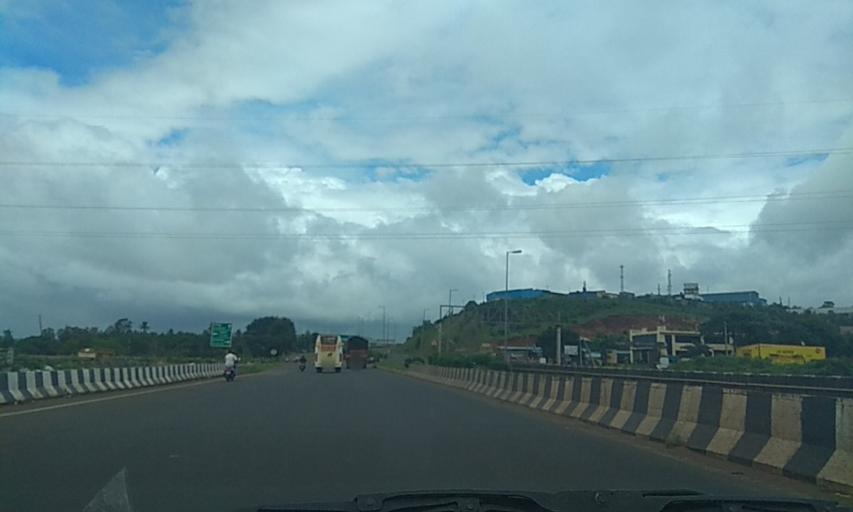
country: IN
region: Karnataka
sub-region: Belgaum
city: Belgaum
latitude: 15.9425
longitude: 74.5241
